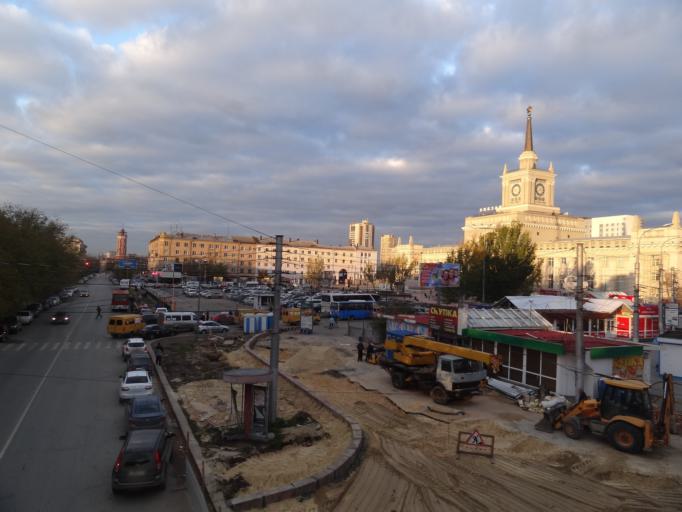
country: RU
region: Volgograd
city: Volgograd
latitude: 48.7123
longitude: 44.5158
